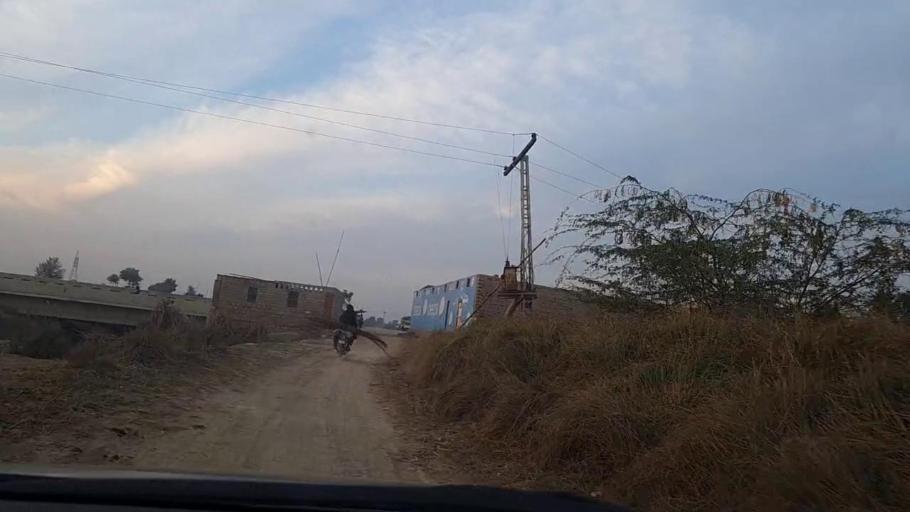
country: PK
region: Sindh
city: Sakrand
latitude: 26.2098
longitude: 68.3252
